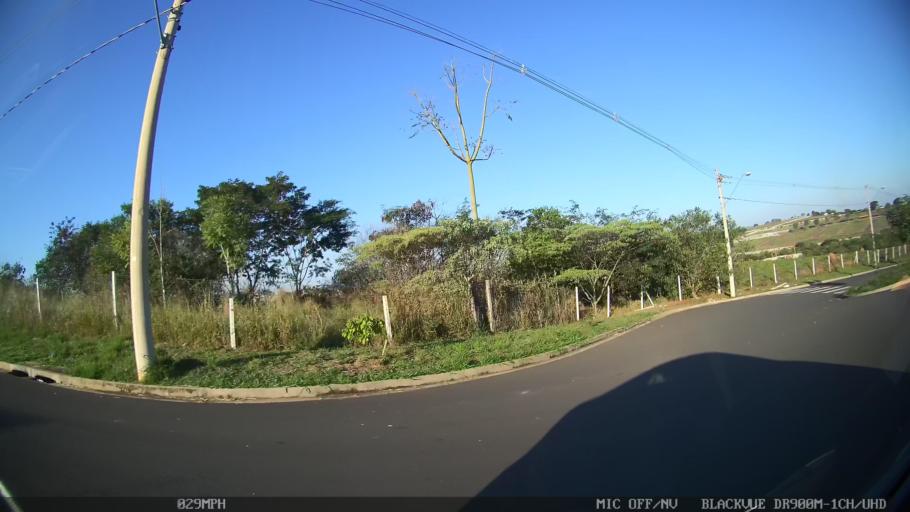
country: BR
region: Sao Paulo
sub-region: Nova Odessa
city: Nova Odessa
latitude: -22.7765
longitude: -47.2764
